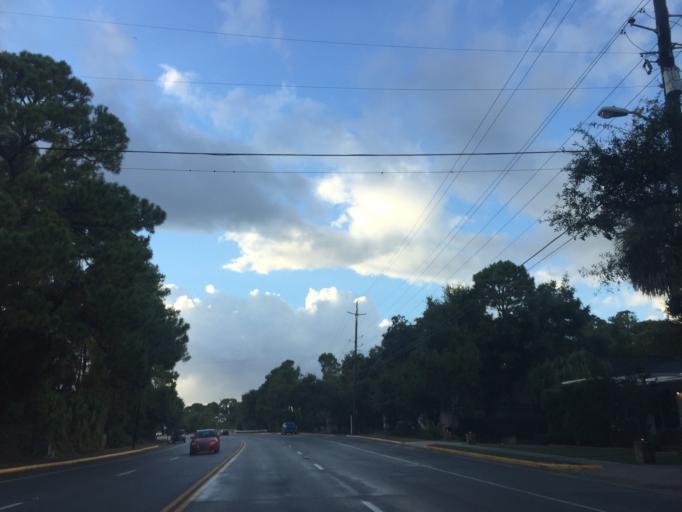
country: US
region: Georgia
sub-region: Chatham County
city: Tybee Island
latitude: 32.0170
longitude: -80.8493
